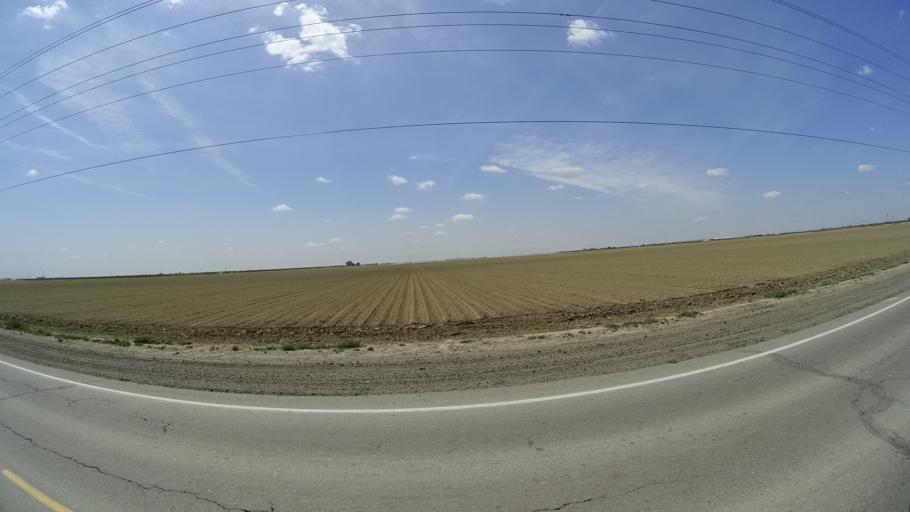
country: US
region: California
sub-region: Tulare County
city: Goshen
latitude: 36.2985
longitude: -119.5151
